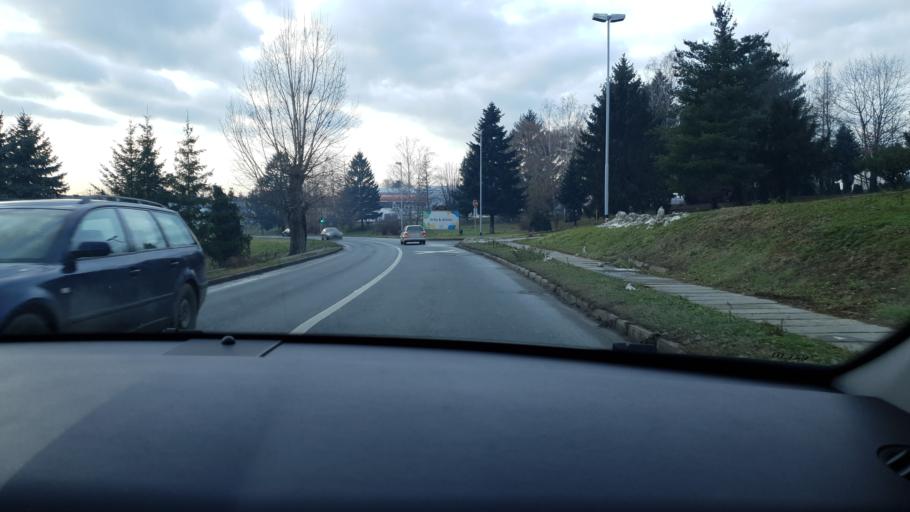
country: HR
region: Pozesko-Slavonska
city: Pozega
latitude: 45.3438
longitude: 17.6899
